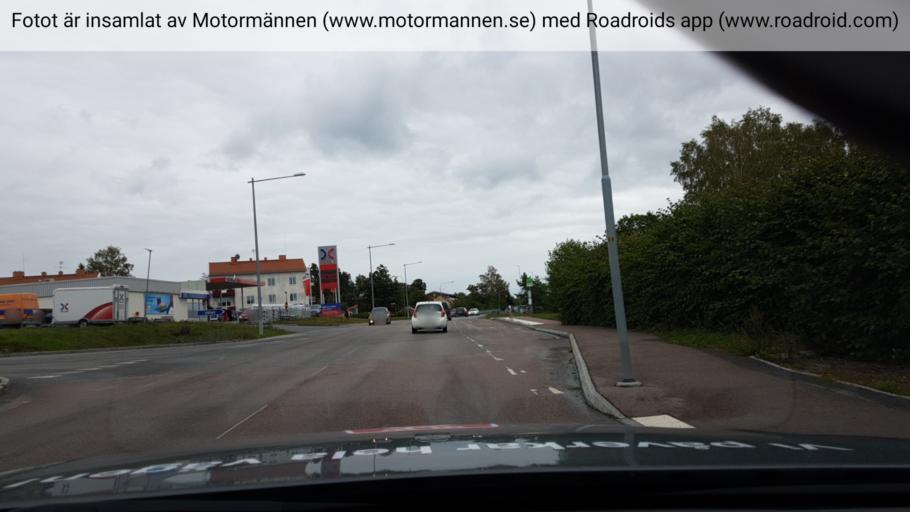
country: SE
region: Soedermanland
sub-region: Trosa Kommun
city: Vagnharad
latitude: 58.9444
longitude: 17.4870
